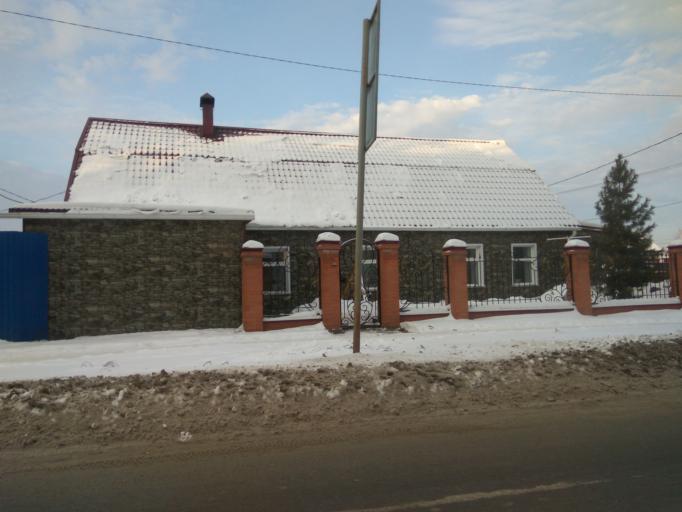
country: RU
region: Kemerovo
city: Yurga
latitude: 55.7174
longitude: 84.9143
